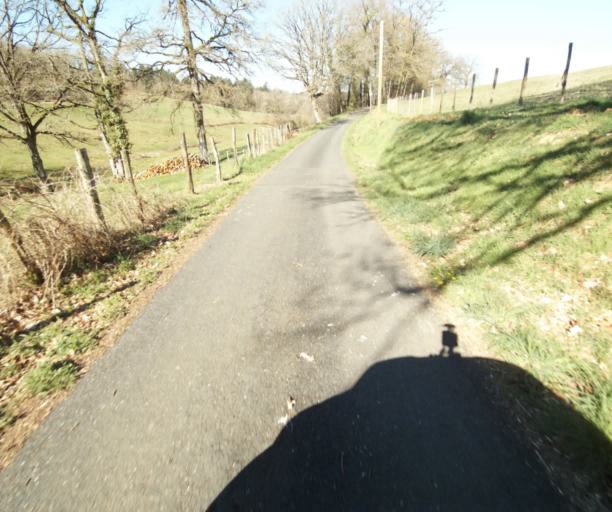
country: FR
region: Limousin
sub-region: Departement de la Correze
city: Chamboulive
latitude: 45.3995
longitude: 1.7005
